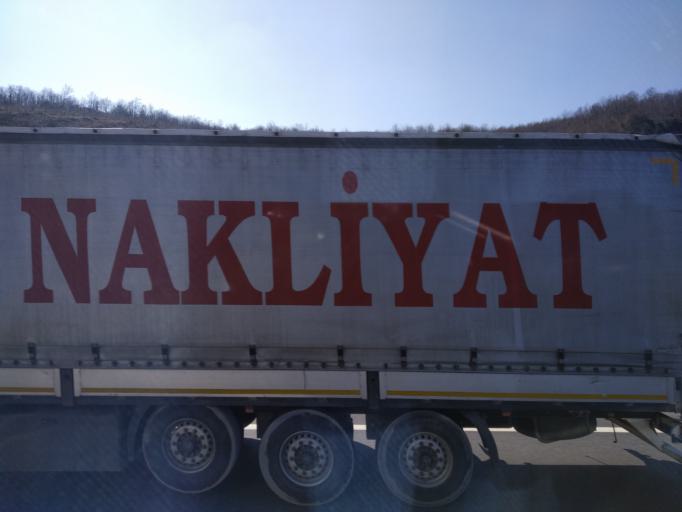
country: TR
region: Istanbul
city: Mahmut Sevket Pasa
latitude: 41.1597
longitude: 29.2610
